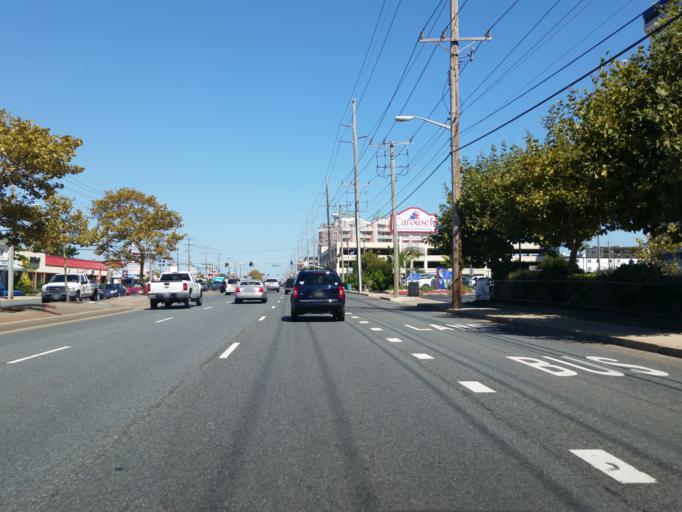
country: US
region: Maryland
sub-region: Worcester County
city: Ocean City
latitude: 38.4219
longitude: -75.0562
